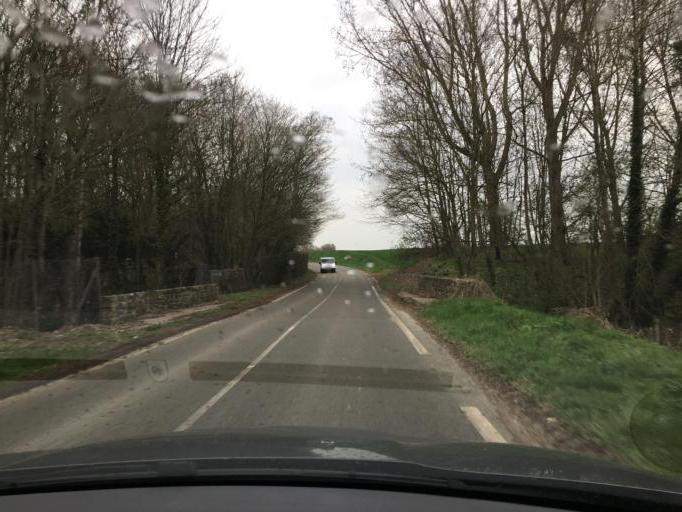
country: FR
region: Ile-de-France
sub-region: Departement des Yvelines
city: Villiers-Saint-Frederic
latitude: 48.8112
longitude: 1.8636
